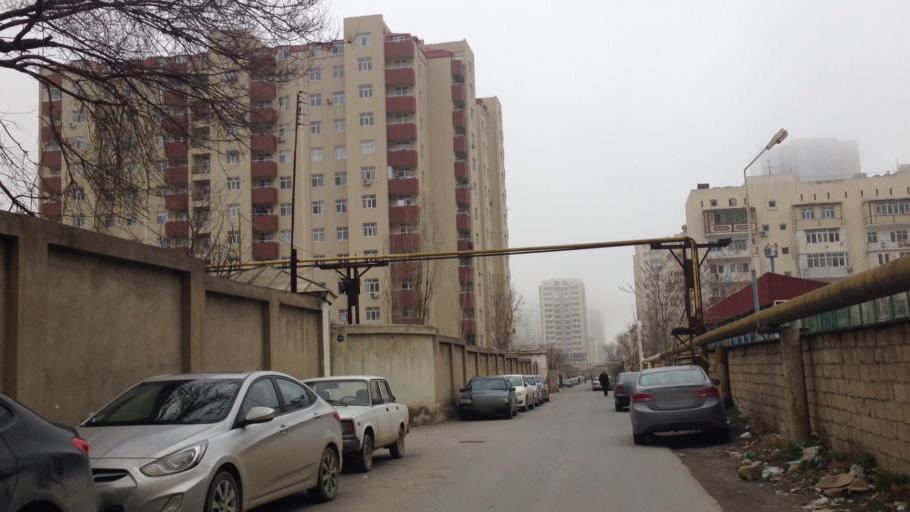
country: AZ
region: Baki
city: Baku
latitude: 40.3873
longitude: 49.8717
